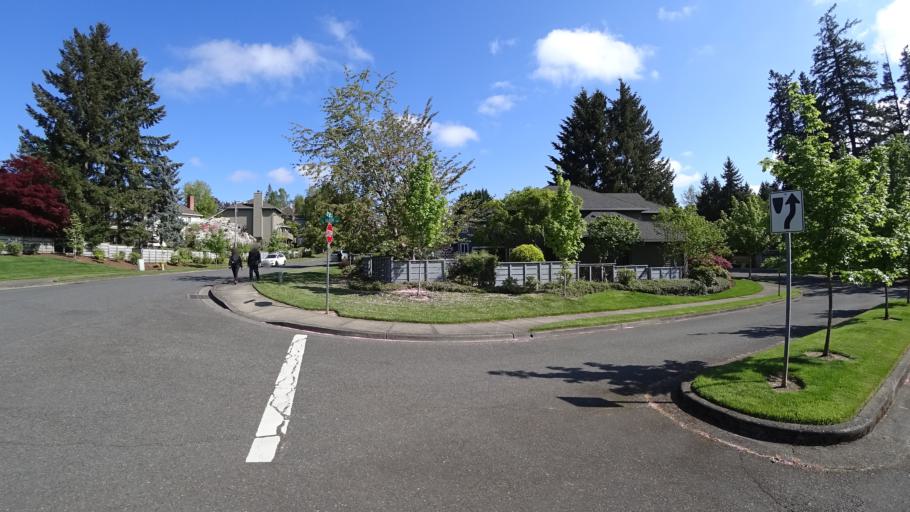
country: US
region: Oregon
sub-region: Washington County
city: King City
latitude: 45.4429
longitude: -122.8327
